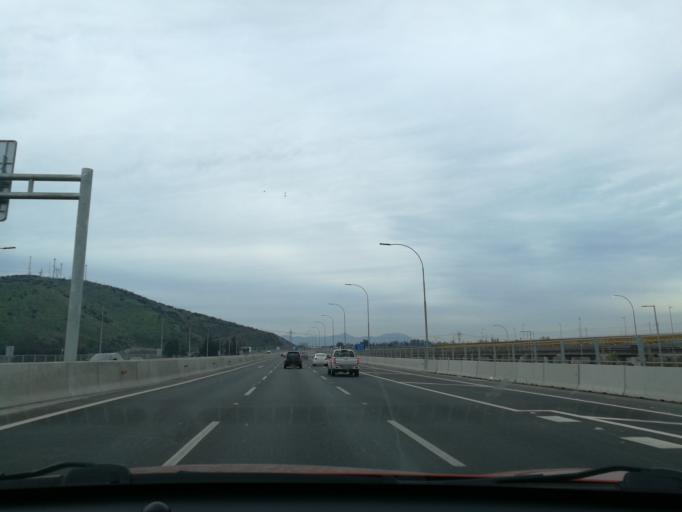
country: CL
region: Santiago Metropolitan
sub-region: Provincia de Maipo
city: Buin
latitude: -33.6944
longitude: -70.7238
